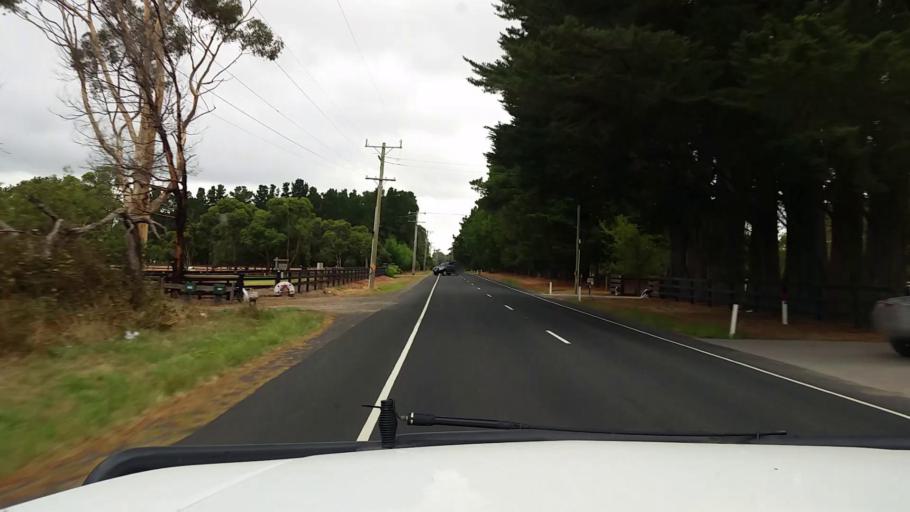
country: AU
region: Victoria
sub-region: Mornington Peninsula
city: Somerville
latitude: -38.2411
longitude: 145.1499
